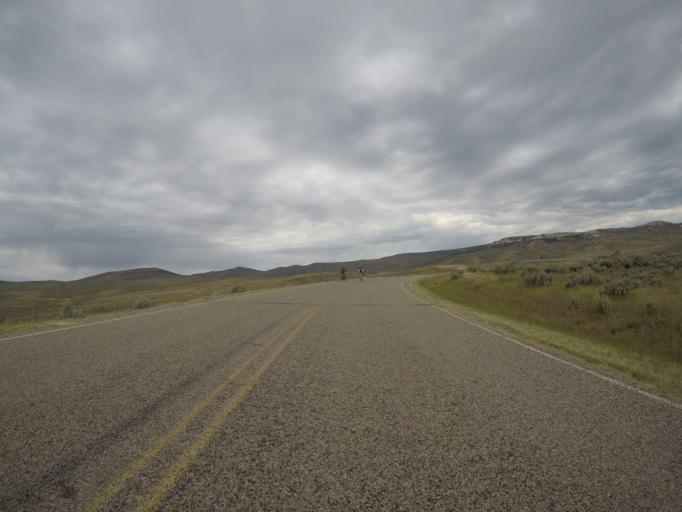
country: US
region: Wyoming
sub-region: Lincoln County
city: Kemmerer
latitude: 41.8358
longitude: -110.7733
